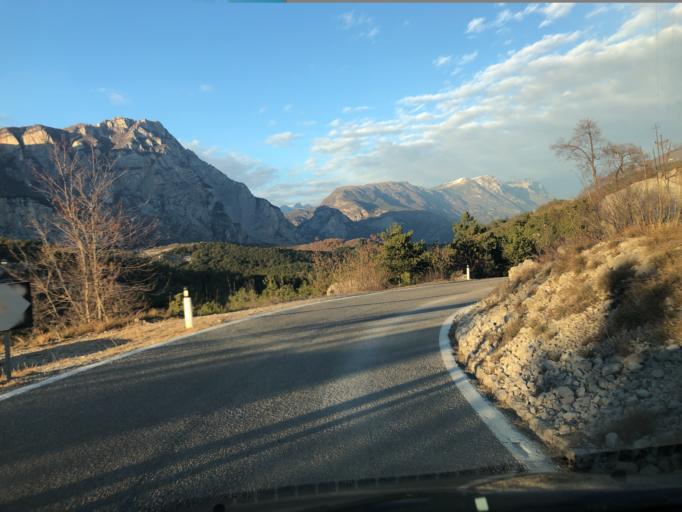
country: IT
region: Trentino-Alto Adige
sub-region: Provincia di Trento
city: Drena
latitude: 45.9855
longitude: 10.9418
